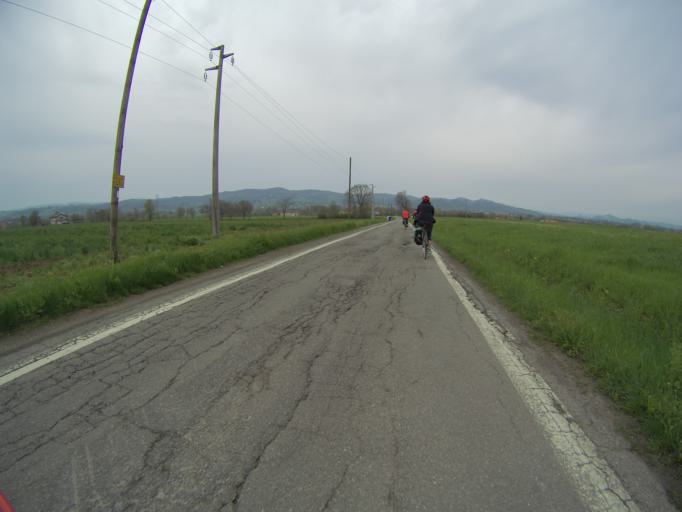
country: IT
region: Emilia-Romagna
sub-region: Provincia di Reggio Emilia
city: Bibbiano
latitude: 44.6578
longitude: 10.4948
